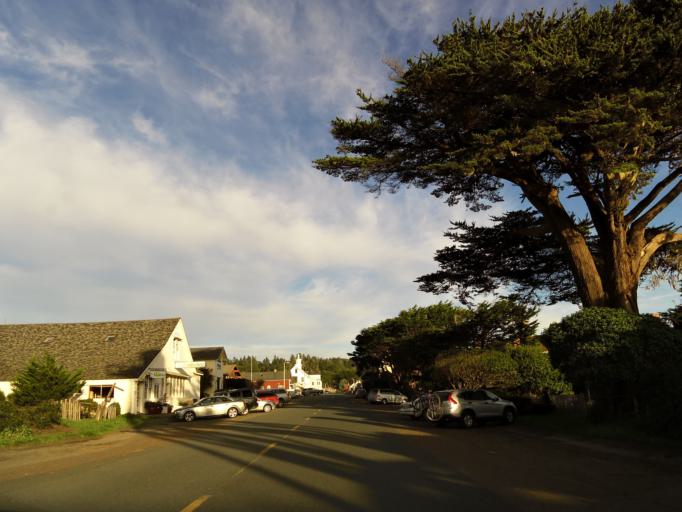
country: US
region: California
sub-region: Mendocino County
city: Fort Bragg
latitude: 39.3058
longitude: -123.8014
